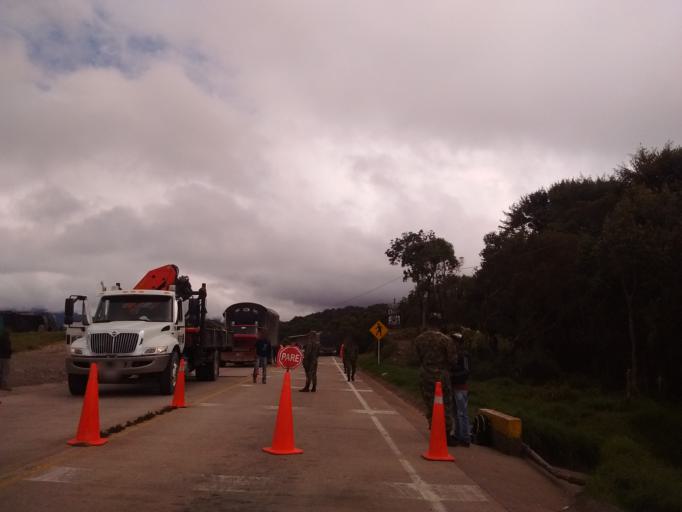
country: CO
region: Huila
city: Isnos
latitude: 2.0565
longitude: -76.3241
